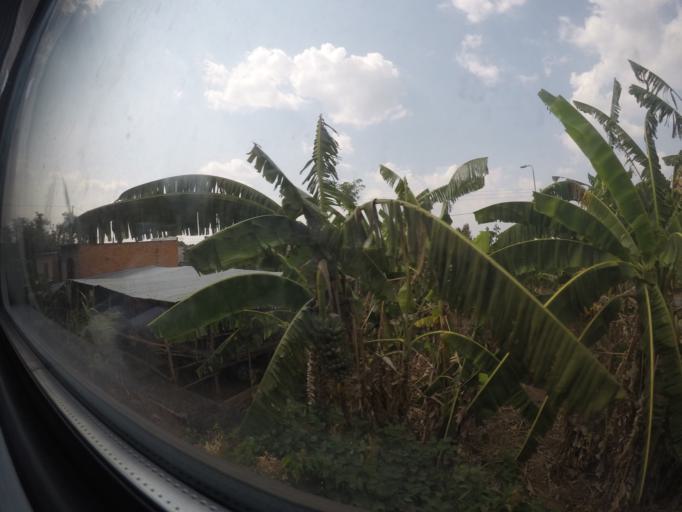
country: VN
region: Dong Nai
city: Gia Ray
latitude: 10.9705
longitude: 107.3863
